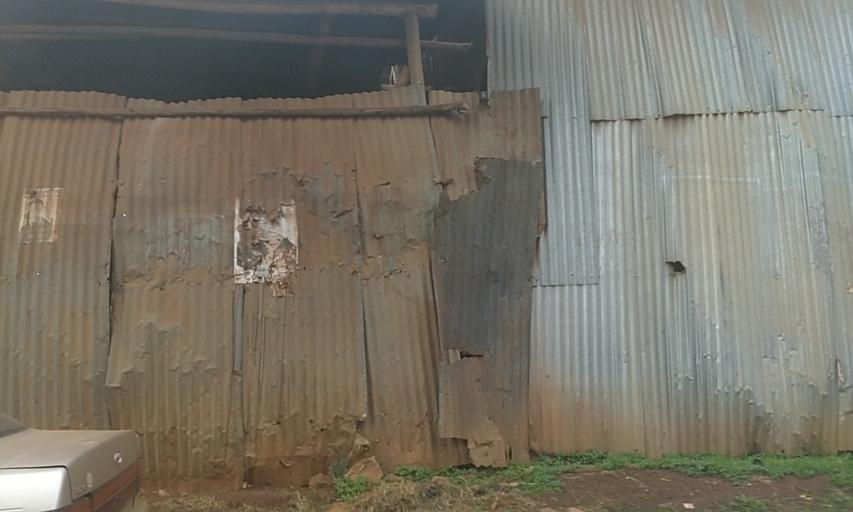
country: UG
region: Central Region
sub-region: Wakiso District
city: Kireka
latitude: 0.3562
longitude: 32.6122
